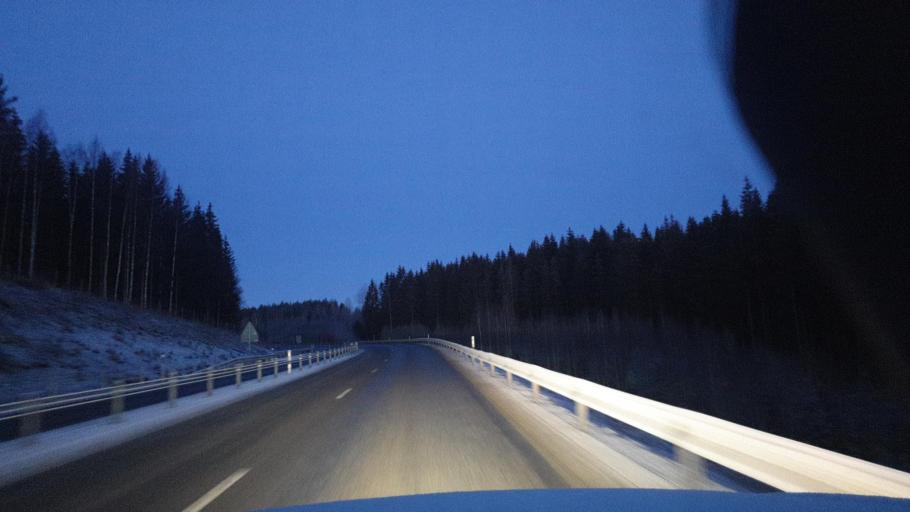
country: SE
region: Vaermland
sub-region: Eda Kommun
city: Amotfors
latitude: 59.7584
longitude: 12.4744
